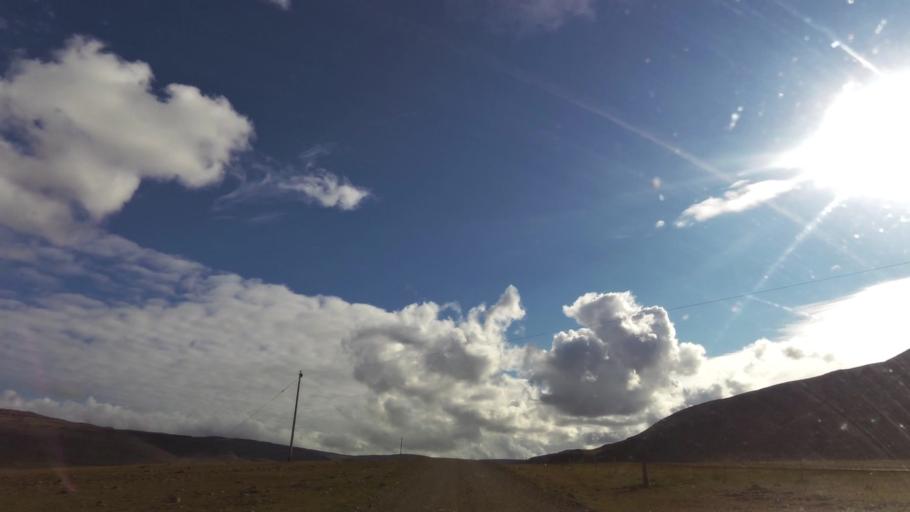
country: IS
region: West
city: Olafsvik
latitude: 65.5882
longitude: -24.1274
